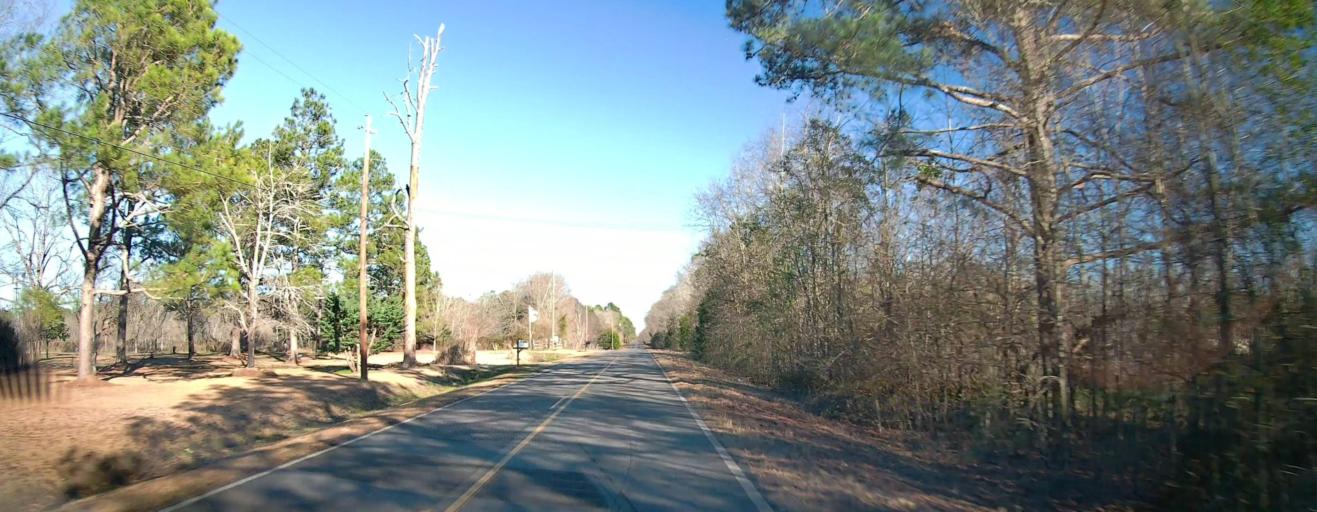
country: US
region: Georgia
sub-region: Sumter County
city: Americus
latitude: 32.0469
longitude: -84.2674
